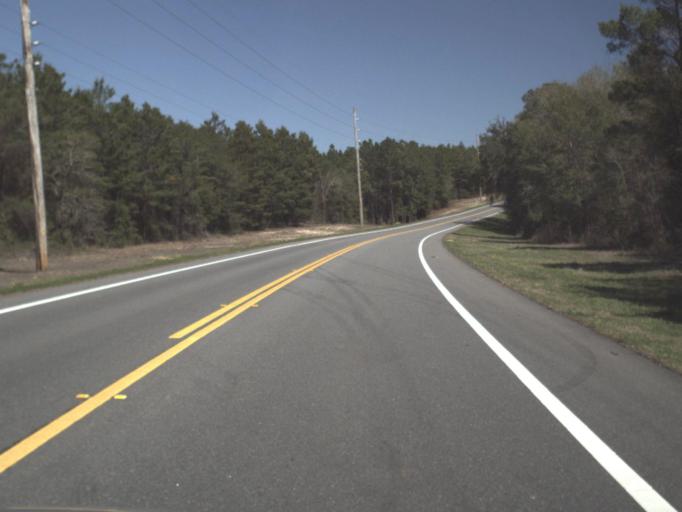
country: US
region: Florida
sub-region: Gadsden County
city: Quincy
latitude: 30.4666
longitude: -84.6380
